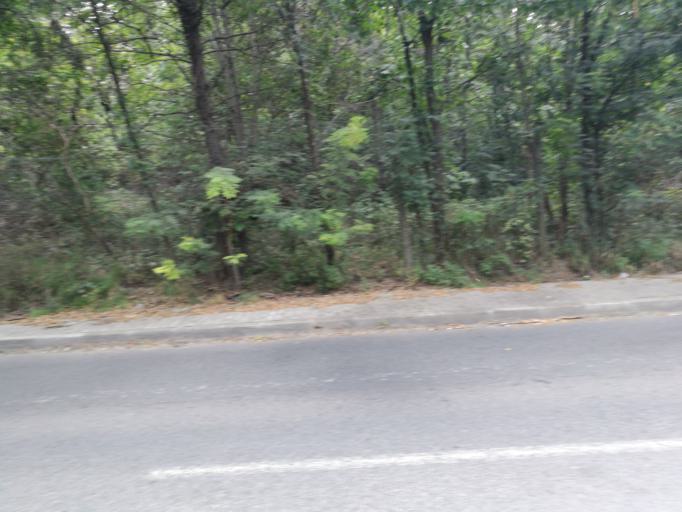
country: RO
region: Iasi
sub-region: Comuna Valea Lupului
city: Valea Lupului
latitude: 47.1735
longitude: 27.5198
